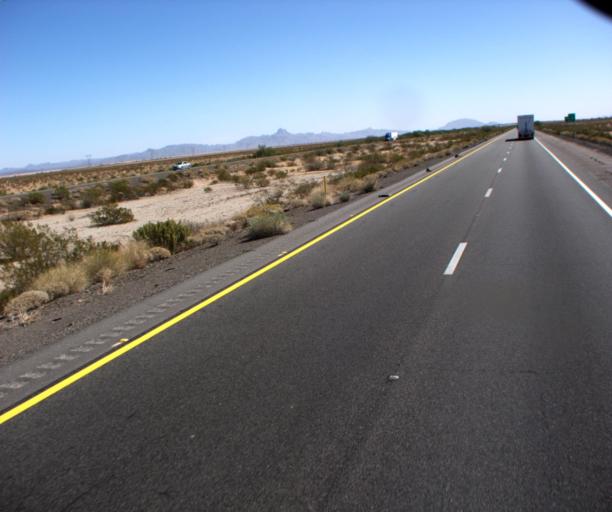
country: US
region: Arizona
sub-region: La Paz County
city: Salome
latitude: 33.5722
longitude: -113.3758
